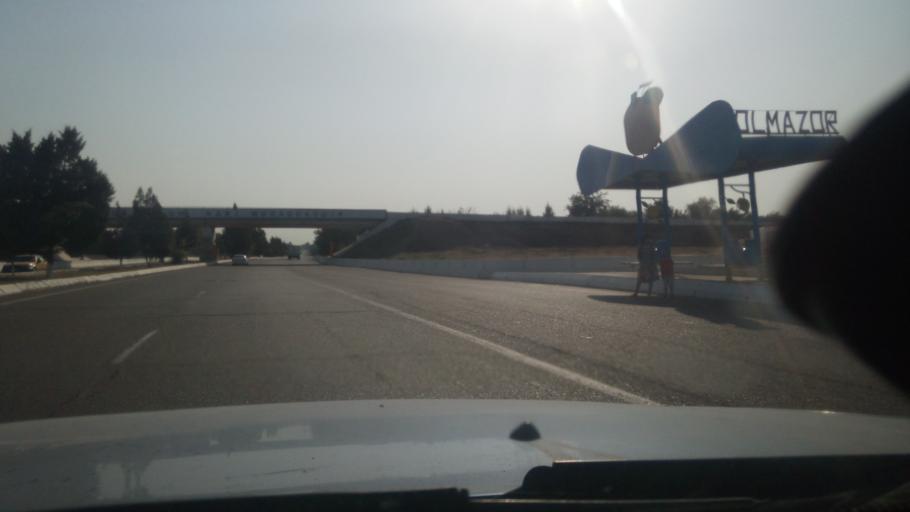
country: UZ
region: Toshkent
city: Zafar
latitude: 41.0127
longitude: 68.8415
